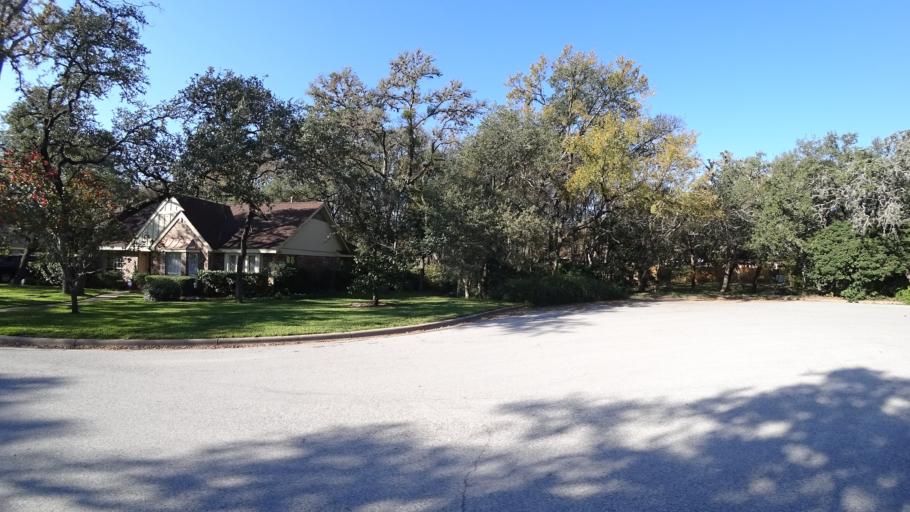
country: US
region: Texas
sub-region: Travis County
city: Shady Hollow
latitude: 30.2221
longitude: -97.8465
